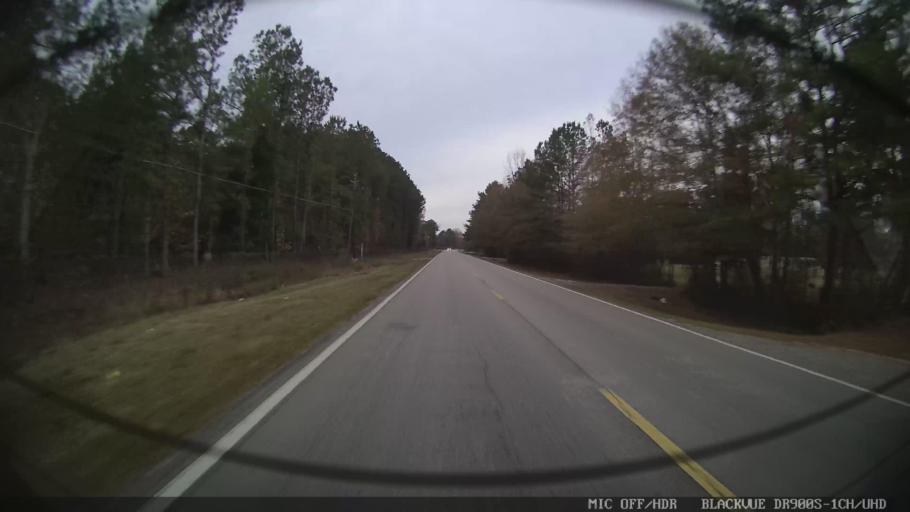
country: US
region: Mississippi
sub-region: Clarke County
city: Stonewall
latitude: 32.0265
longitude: -88.8593
